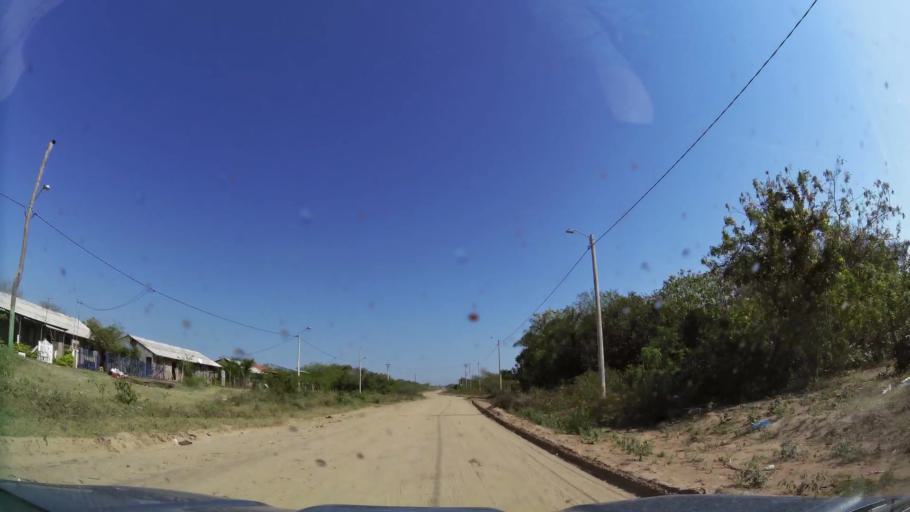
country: BO
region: Santa Cruz
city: Cotoca
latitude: -17.7227
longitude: -63.0686
